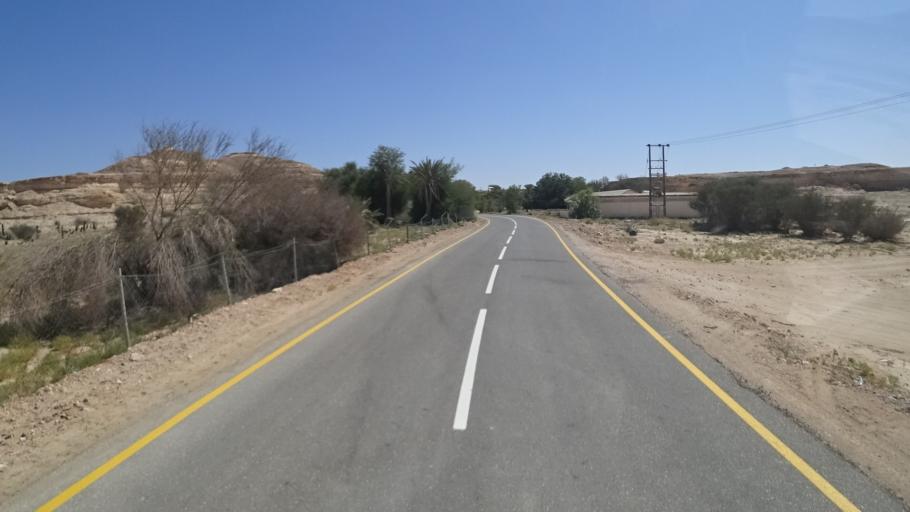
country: OM
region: Zufar
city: Salalah
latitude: 17.4797
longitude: 53.3515
